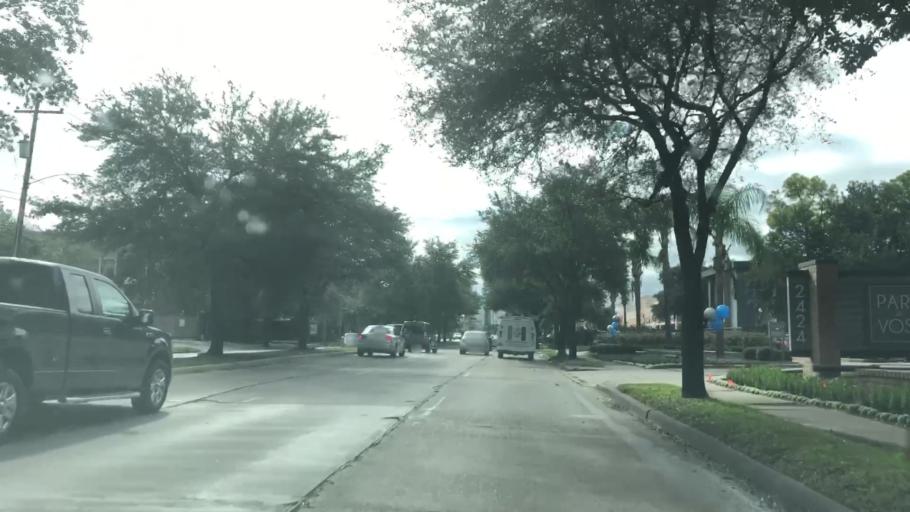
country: US
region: Texas
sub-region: Harris County
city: Piney Point Village
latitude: 29.7418
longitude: -95.5010
